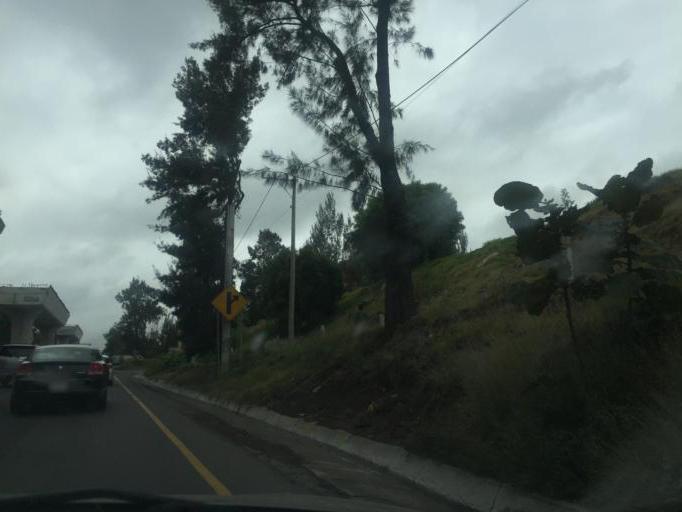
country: MX
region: Mexico City
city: Tlalpan
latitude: 19.2590
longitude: -99.1630
